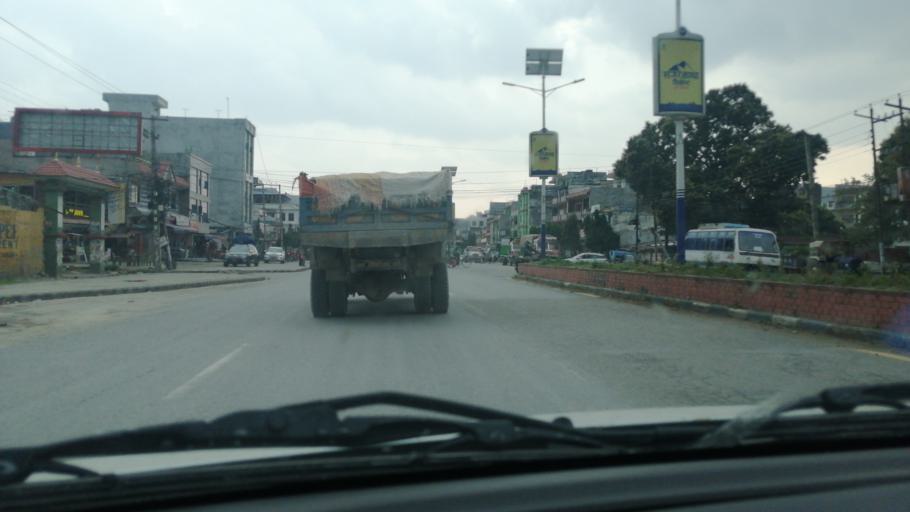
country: NP
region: Western Region
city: Butwal
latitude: 27.7070
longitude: 83.4676
